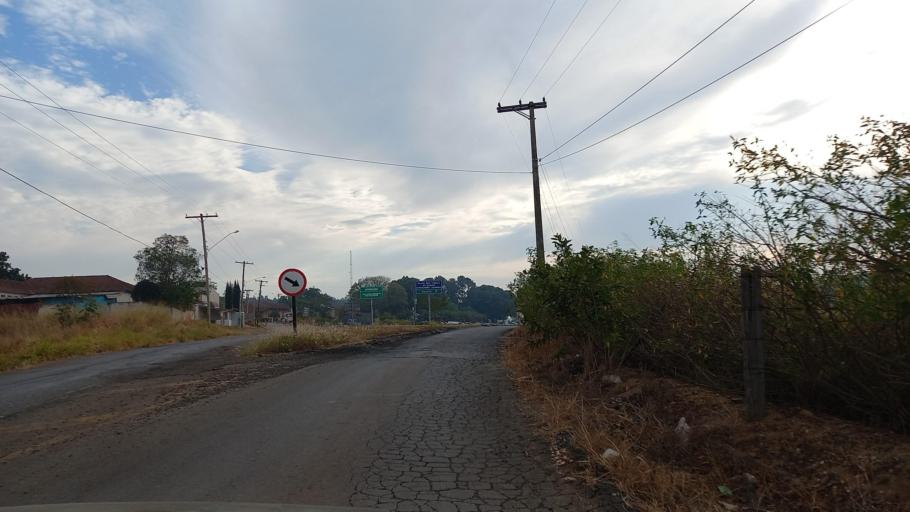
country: BR
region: Sao Paulo
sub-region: Moji-Guacu
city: Mogi-Gaucu
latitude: -22.3331
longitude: -46.8811
